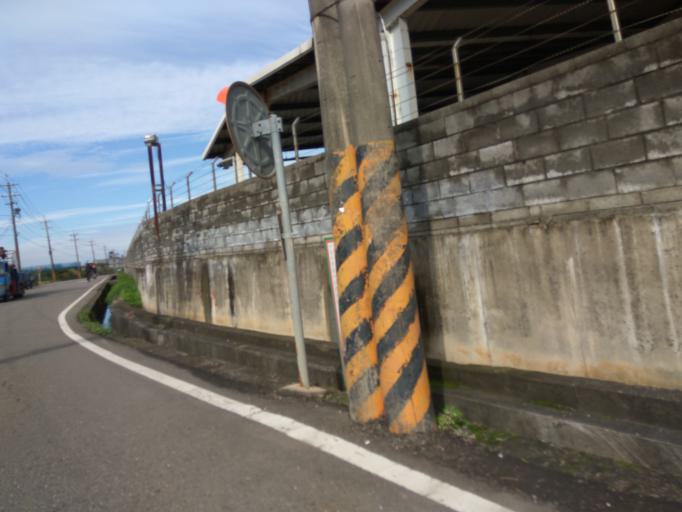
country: TW
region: Taiwan
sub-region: Hsinchu
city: Zhubei
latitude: 24.9920
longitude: 121.0985
